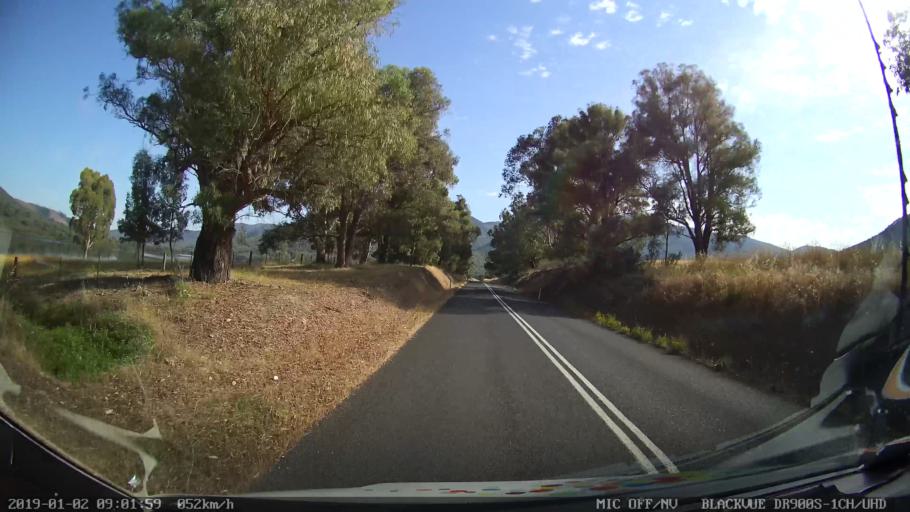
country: AU
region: New South Wales
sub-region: Tumut Shire
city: Tumut
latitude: -35.5765
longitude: 148.3102
